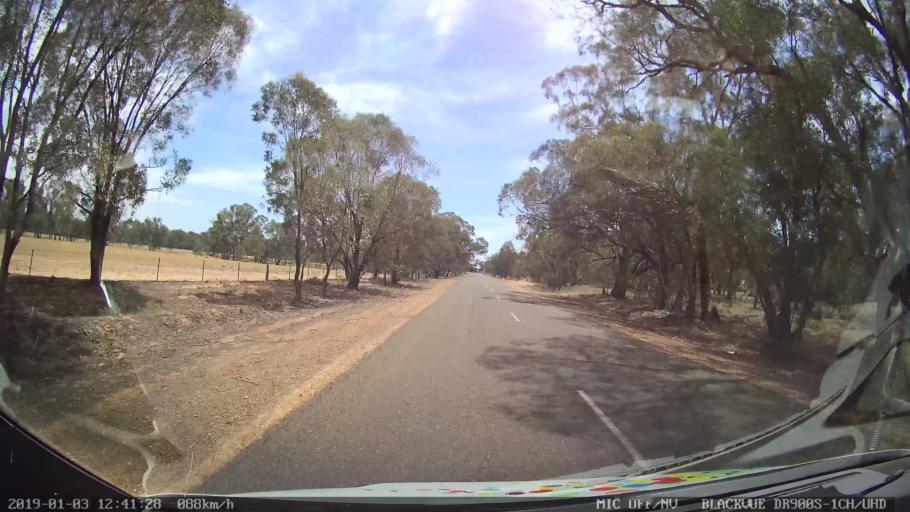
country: AU
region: New South Wales
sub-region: Weddin
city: Grenfell
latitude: -33.7992
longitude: 148.2150
